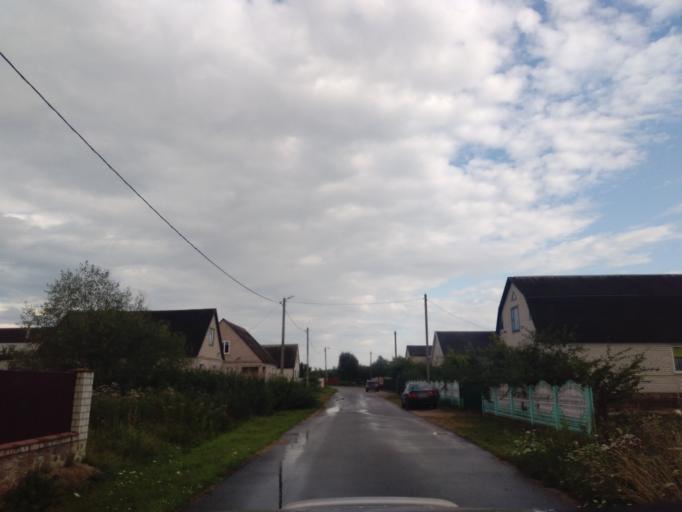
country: BY
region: Minsk
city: Kapyl'
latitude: 53.1596
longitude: 27.0741
